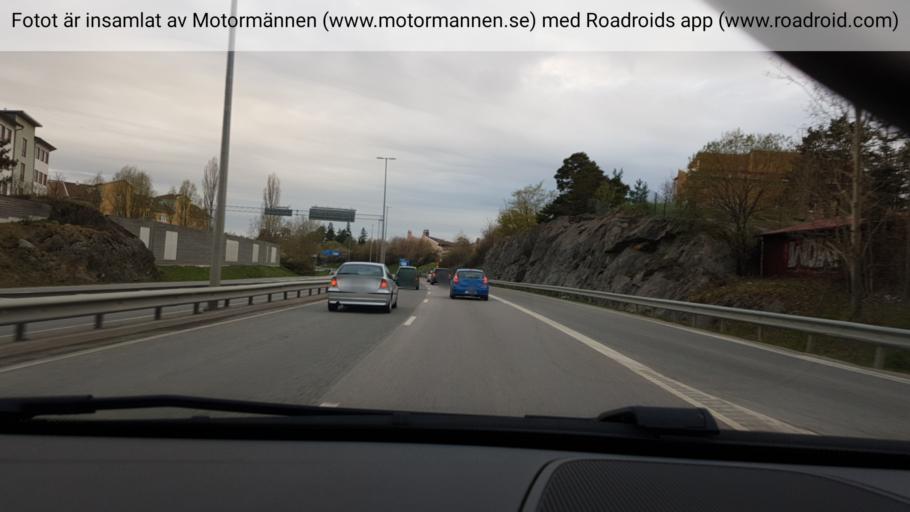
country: SE
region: Stockholm
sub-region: Huddinge Kommun
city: Huddinge
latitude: 59.2398
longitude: 17.9782
